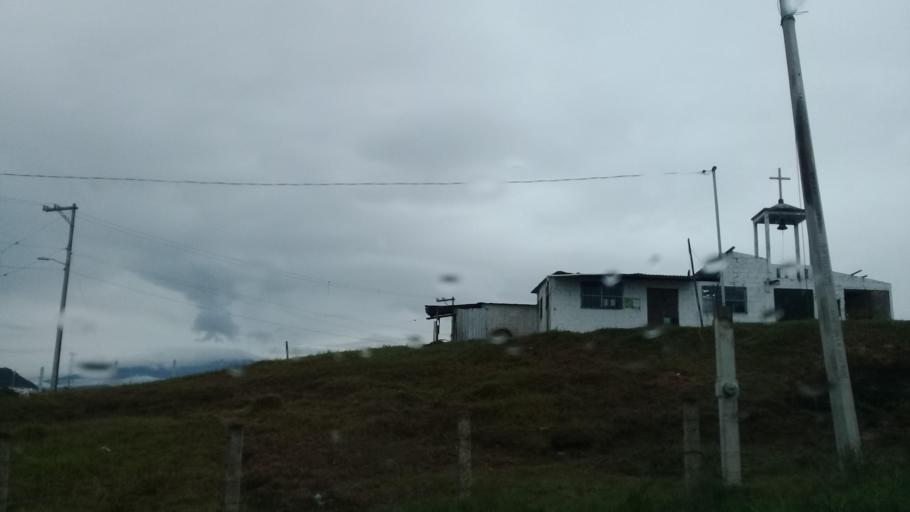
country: MX
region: Veracruz
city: El Castillo
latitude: 19.5676
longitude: -96.8857
